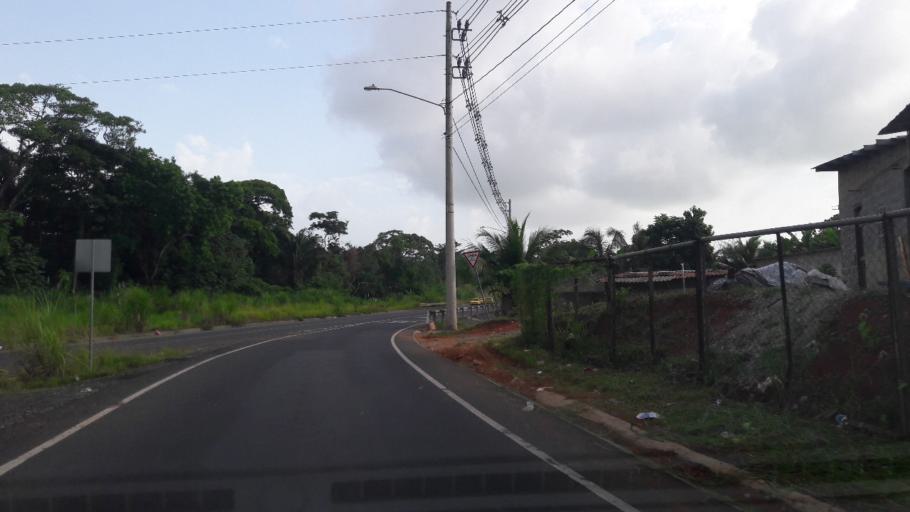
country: PA
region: Colon
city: Cativa
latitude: 9.3546
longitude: -79.8597
